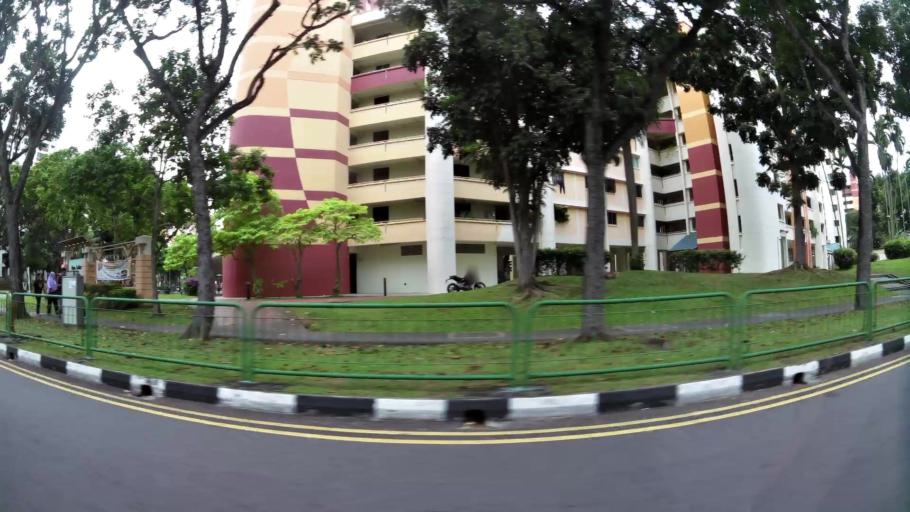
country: SG
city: Singapore
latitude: 1.3528
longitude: 103.8893
